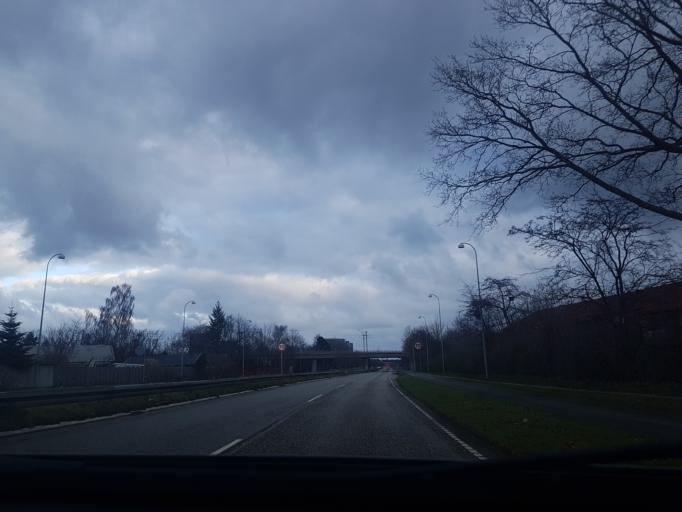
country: DK
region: Capital Region
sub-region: Vallensbaek Kommune
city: Vallensbaek
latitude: 55.6219
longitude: 12.3823
